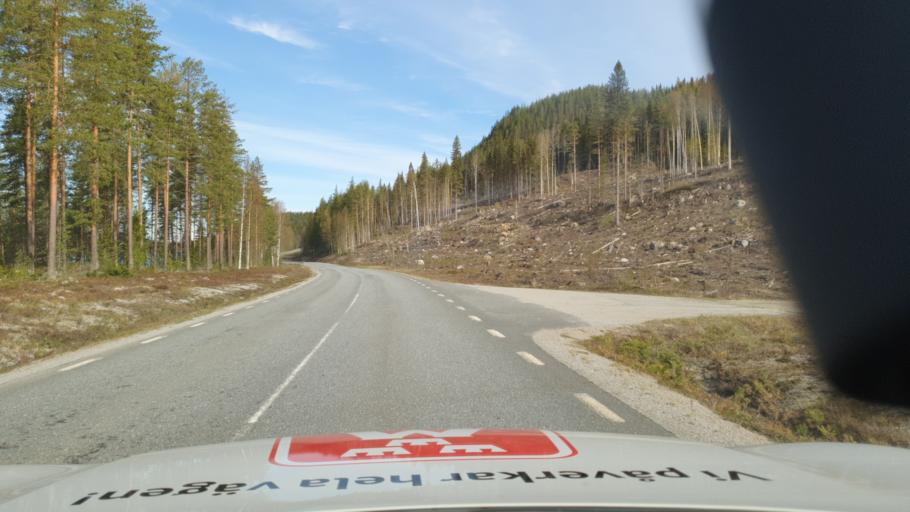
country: SE
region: Vaesterbotten
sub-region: Lycksele Kommun
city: Lycksele
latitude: 64.4149
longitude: 19.0144
